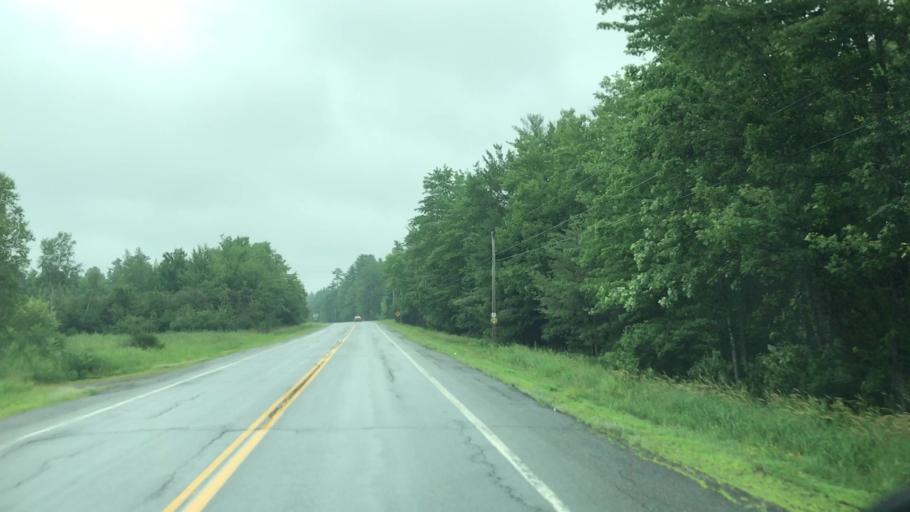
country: US
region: Maine
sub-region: Penobscot County
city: Howland
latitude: 45.2491
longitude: -68.6387
